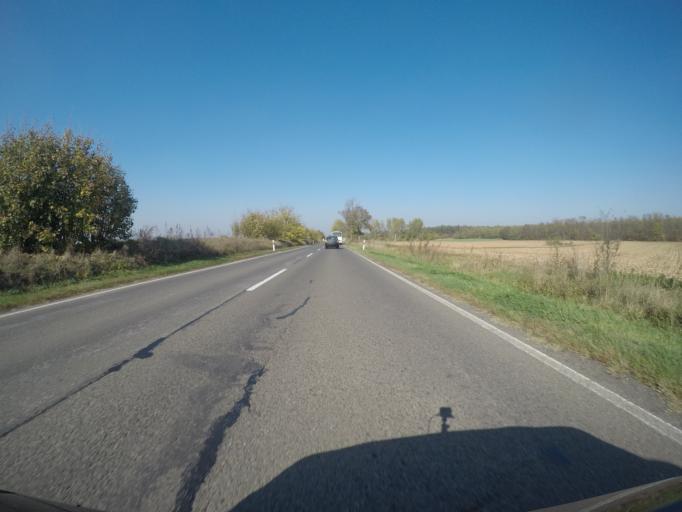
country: HU
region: Tolna
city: Szedres
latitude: 46.5031
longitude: 18.6692
